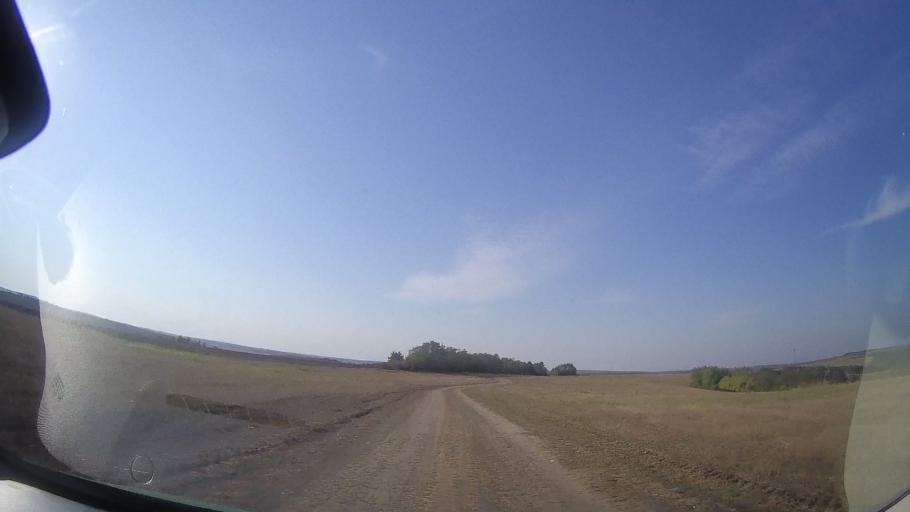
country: RO
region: Timis
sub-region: Comuna Bogda
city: Bogda
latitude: 45.8885
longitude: 21.5590
